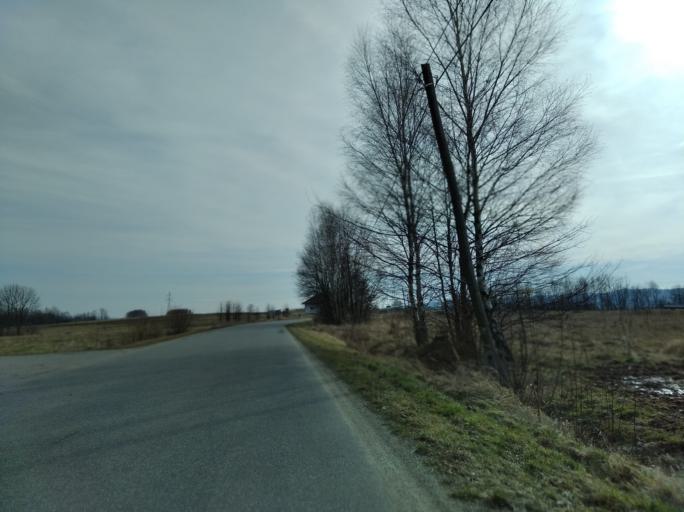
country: PL
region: Subcarpathian Voivodeship
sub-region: Powiat brzozowski
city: Jasienica Rosielna
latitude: 49.7451
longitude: 21.9415
